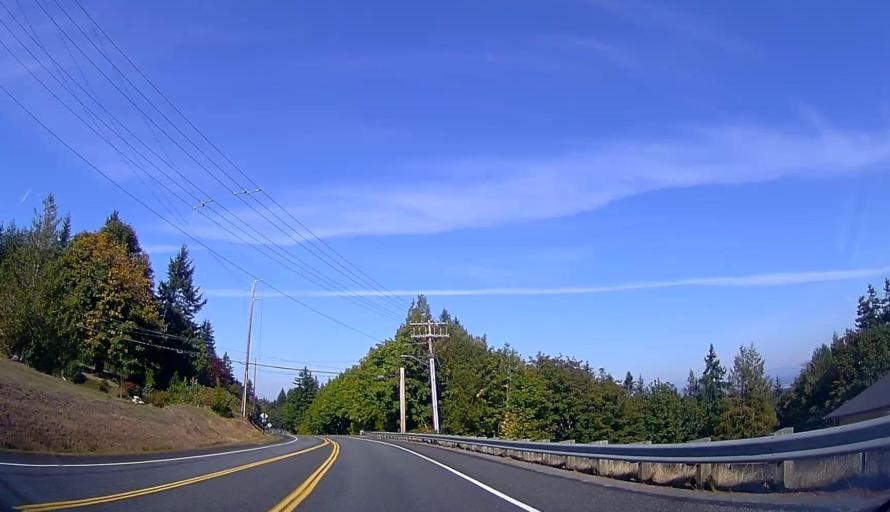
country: US
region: Washington
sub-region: Island County
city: Camano
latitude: 48.1961
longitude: -122.4853
